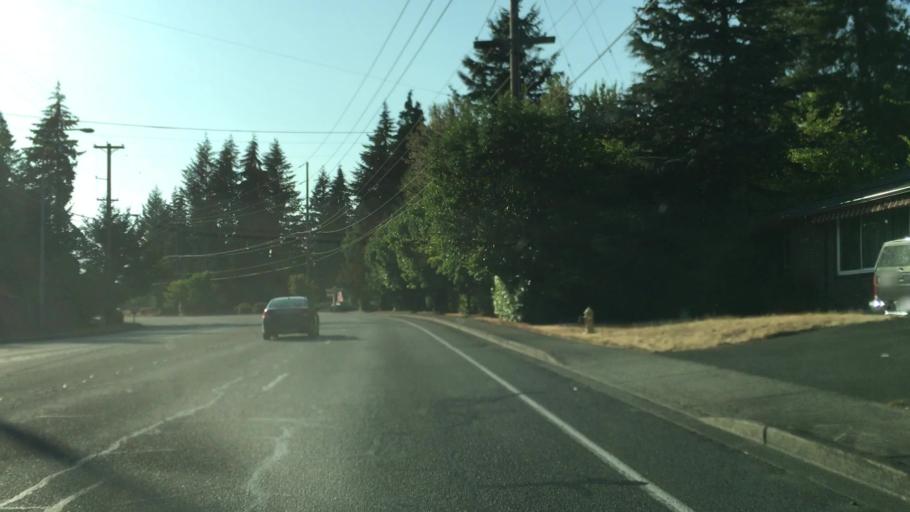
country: US
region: Washington
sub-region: Pierce County
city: Fife Heights
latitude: 47.2823
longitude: -122.3460
